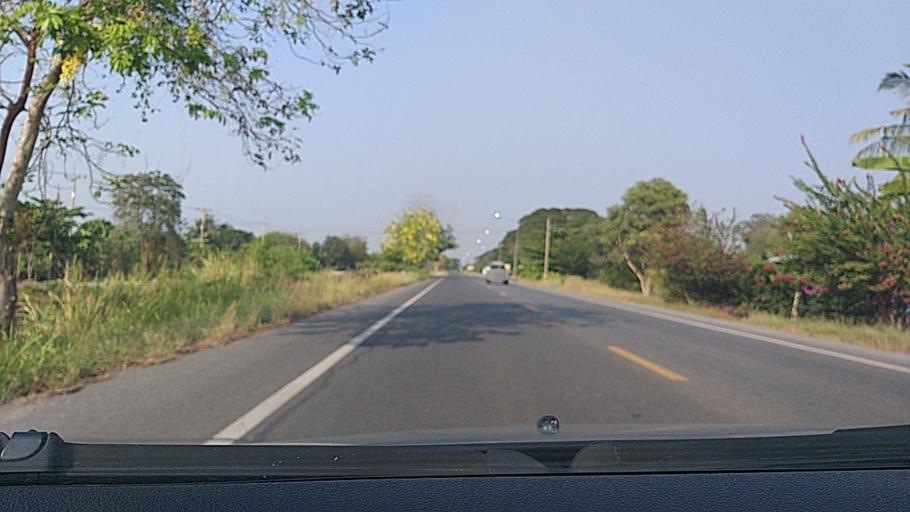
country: TH
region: Sing Buri
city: Phrom Buri
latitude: 14.7418
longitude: 100.4383
